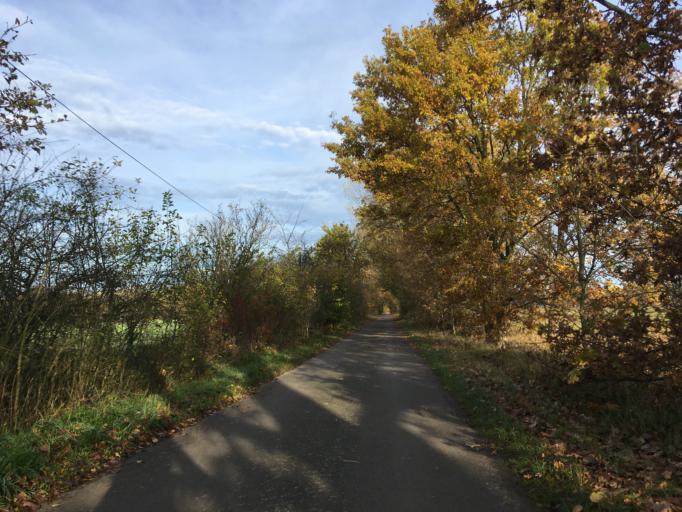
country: DE
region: Brandenburg
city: Luebben
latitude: 51.9819
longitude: 13.8733
